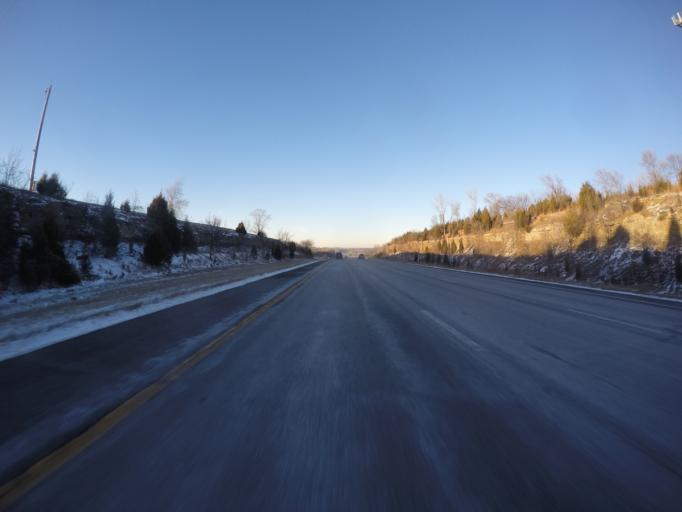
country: US
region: Kansas
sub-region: Wyandotte County
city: Edwardsville
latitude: 39.0331
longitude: -94.7874
